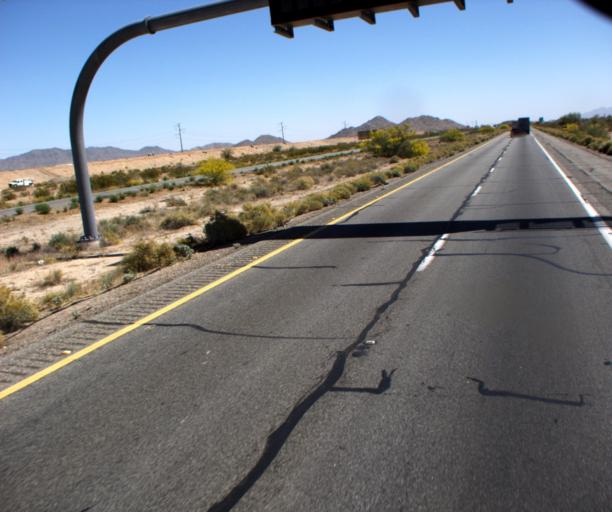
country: US
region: Arizona
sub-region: Maricopa County
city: Buckeye
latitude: 33.4368
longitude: -112.6673
